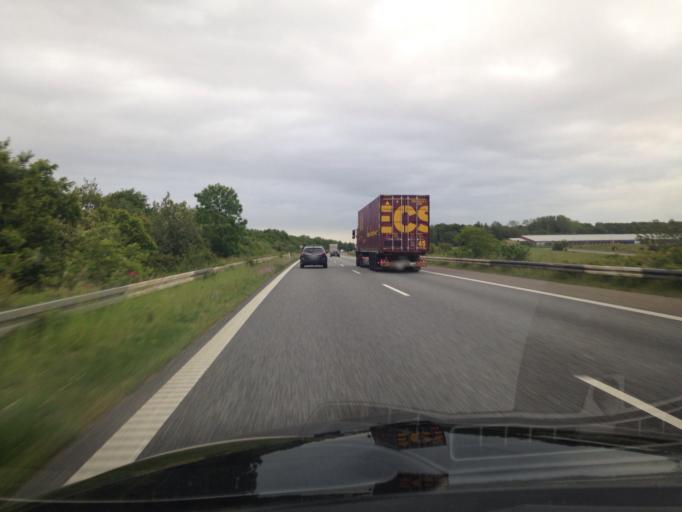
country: DK
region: South Denmark
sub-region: Fredericia Kommune
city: Taulov
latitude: 55.5396
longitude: 9.6606
